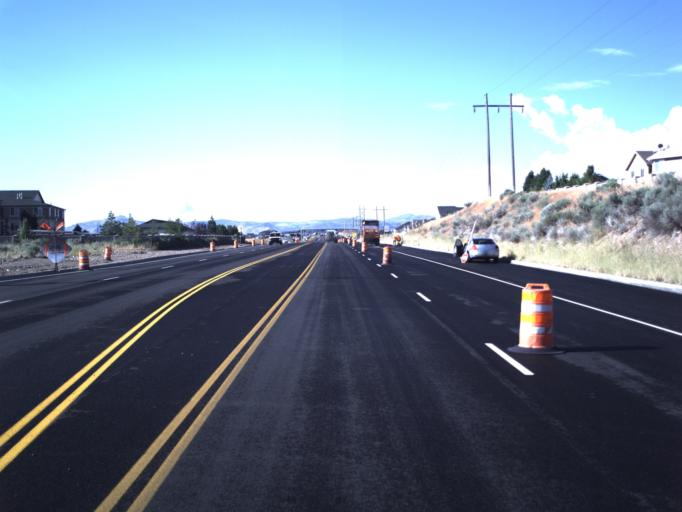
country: US
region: Utah
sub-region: Salt Lake County
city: Oquirrh
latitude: 40.6083
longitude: -112.0558
